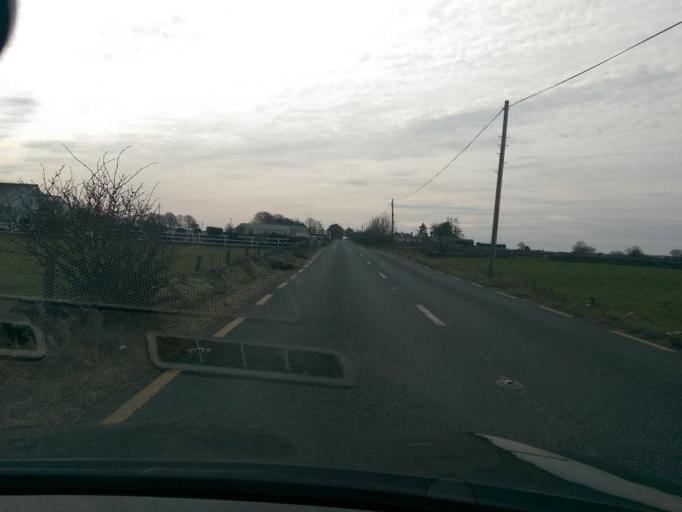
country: IE
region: Connaught
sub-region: County Galway
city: Tuam
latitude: 53.3963
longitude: -8.8362
